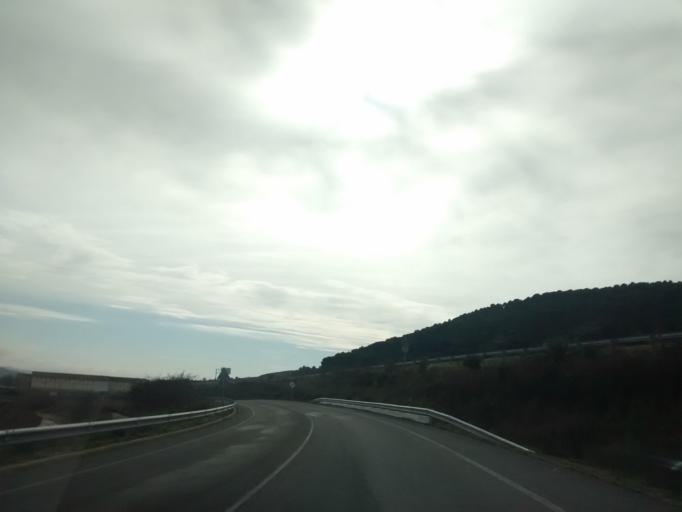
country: ES
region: Navarre
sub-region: Provincia de Navarra
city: Carcar
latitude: 42.3831
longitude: -1.9641
